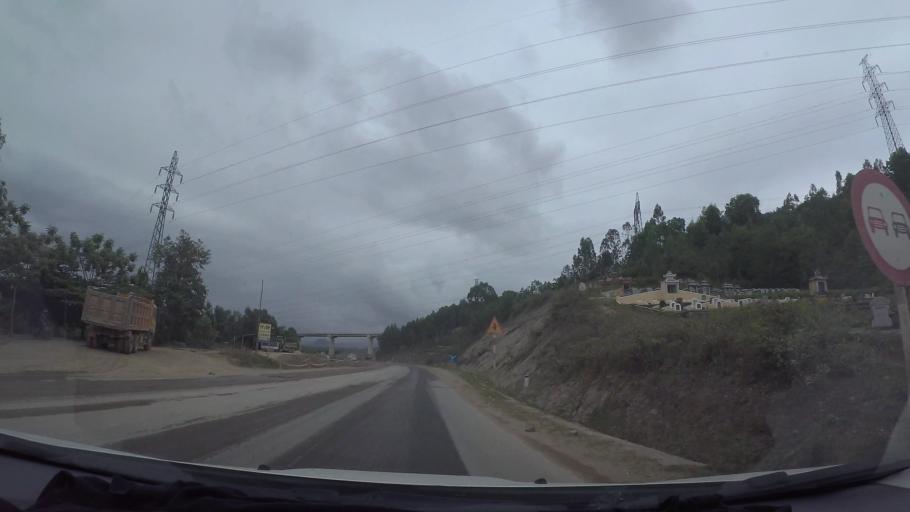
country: VN
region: Da Nang
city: Lien Chieu
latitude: 16.1000
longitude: 108.0924
